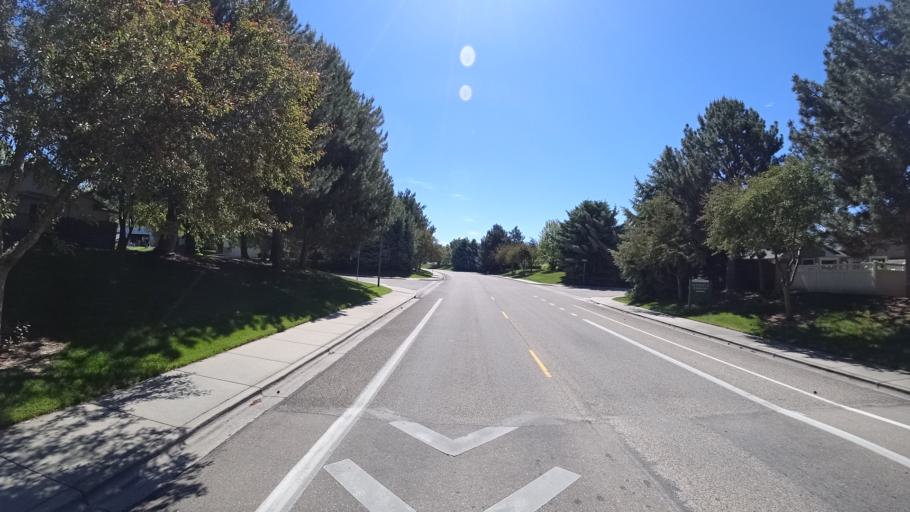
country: US
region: Idaho
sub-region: Ada County
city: Boise
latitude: 43.5521
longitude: -116.1334
